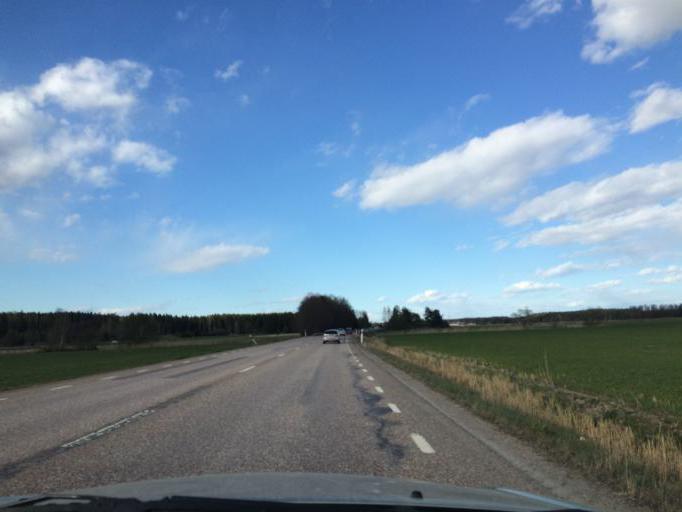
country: SE
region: Vaestmanland
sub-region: Hallstahammars Kommun
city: Kolback
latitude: 59.5457
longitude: 16.3302
